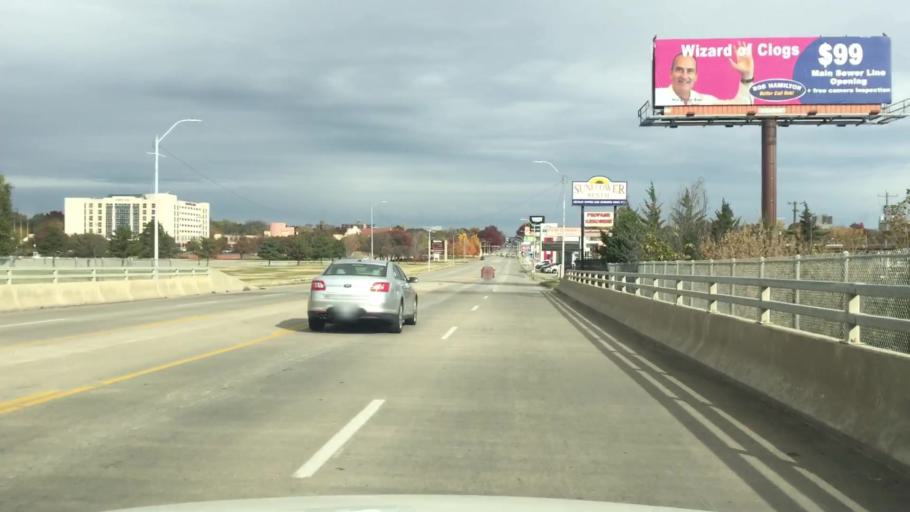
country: US
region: Kansas
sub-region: Shawnee County
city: Topeka
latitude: 39.0314
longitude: -95.6828
